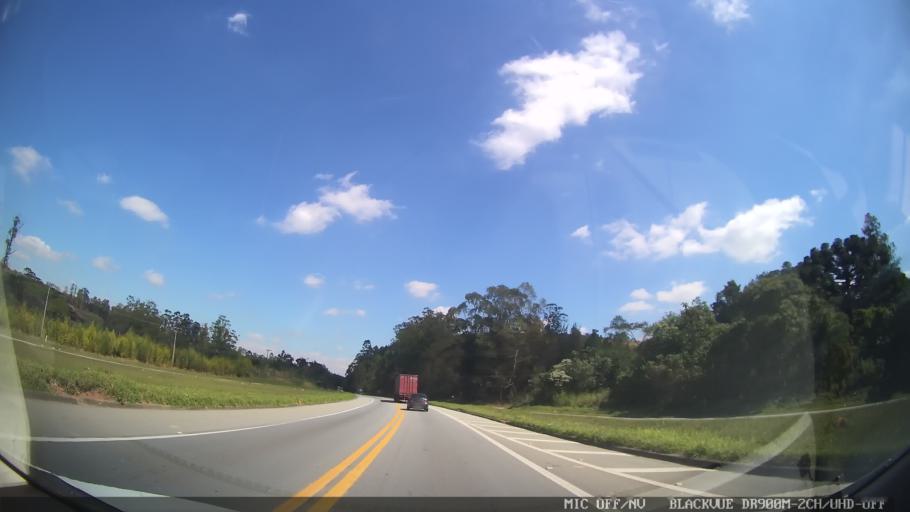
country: BR
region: Sao Paulo
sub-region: Francisco Morato
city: Francisco Morato
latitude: -23.2855
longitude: -46.8000
